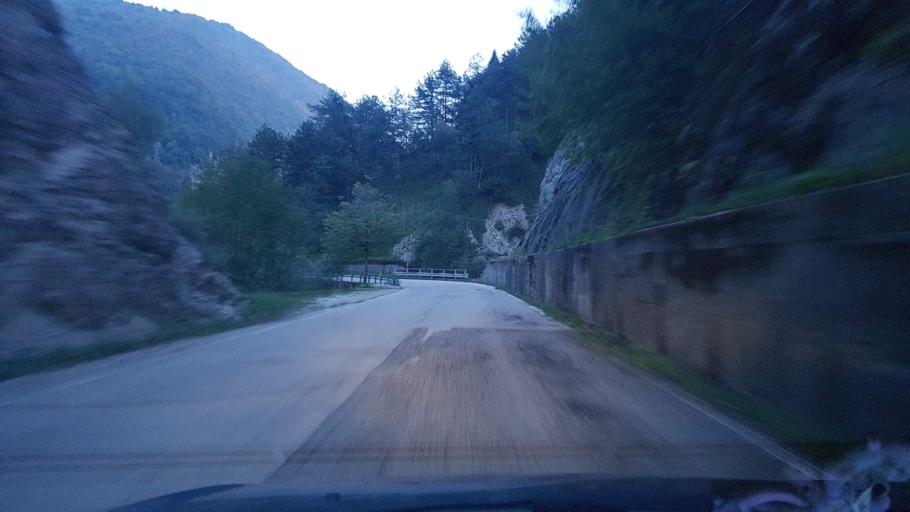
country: IT
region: Friuli Venezia Giulia
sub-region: Provincia di Pordenone
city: Frisanco
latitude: 46.2426
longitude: 12.7442
